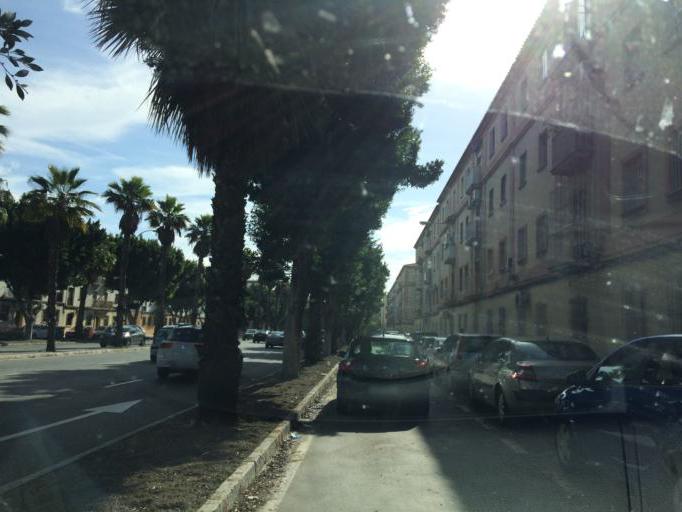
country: ES
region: Andalusia
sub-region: Provincia de Malaga
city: Malaga
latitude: 36.7155
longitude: -4.4453
